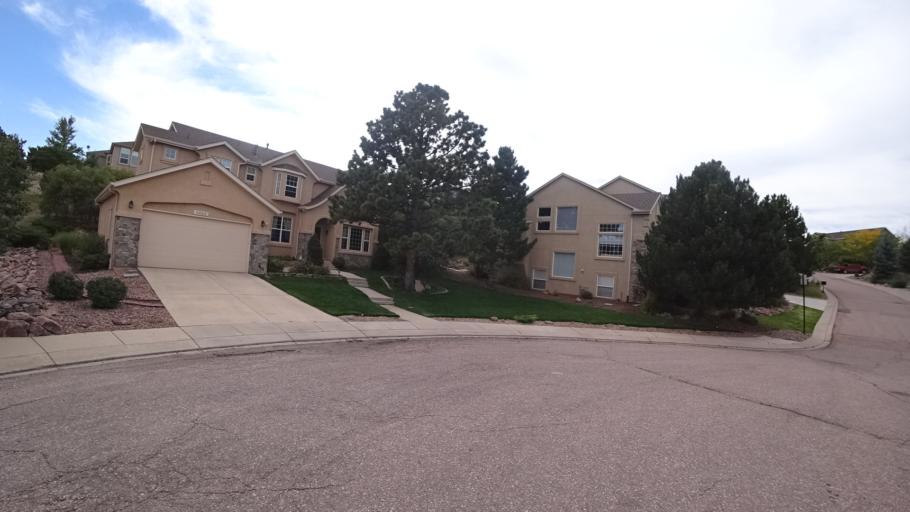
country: US
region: Colorado
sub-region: El Paso County
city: Colorado Springs
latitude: 38.9009
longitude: -104.7870
